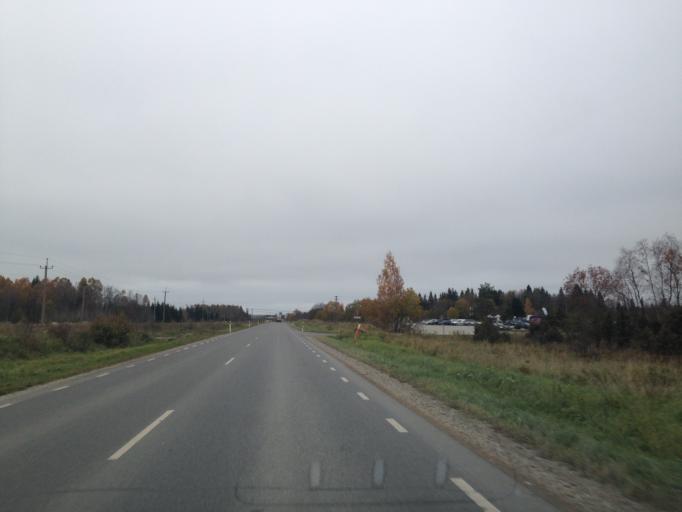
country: EE
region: Harju
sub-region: Harku vald
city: Tabasalu
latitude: 59.4098
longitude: 24.5460
